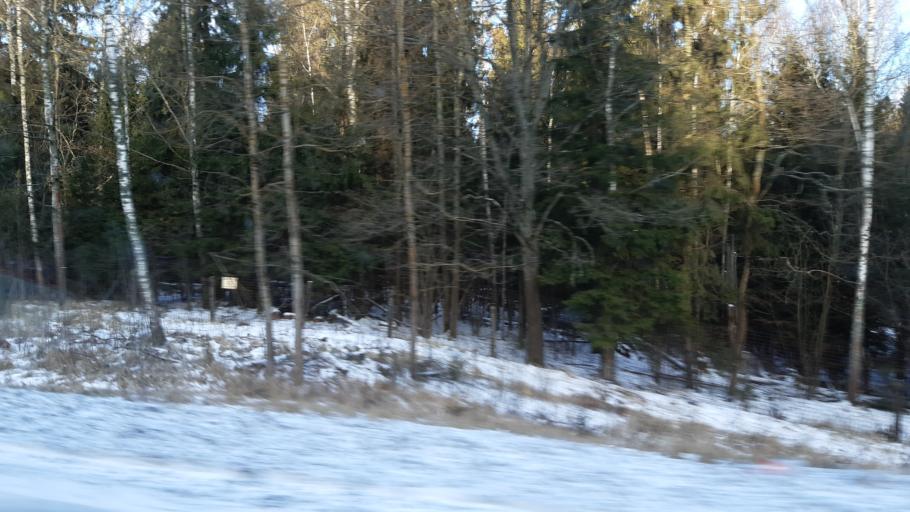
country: RU
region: Vladimir
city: Arsaki
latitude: 56.2659
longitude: 38.4280
